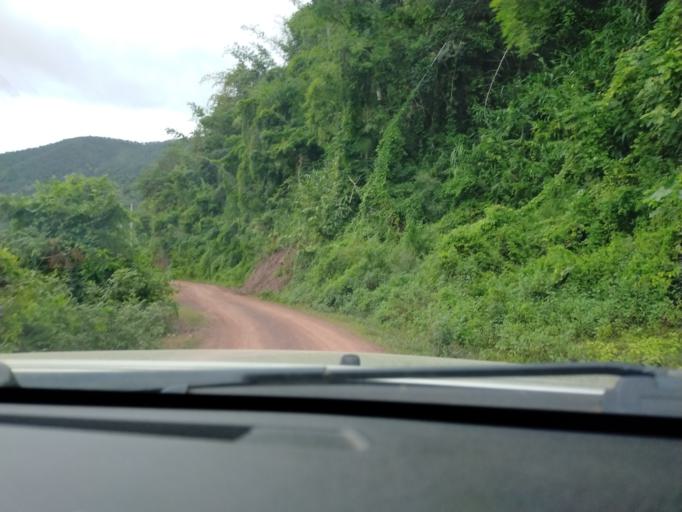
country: TH
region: Nan
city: Chaloem Phra Kiat
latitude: 19.7746
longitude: 101.3533
